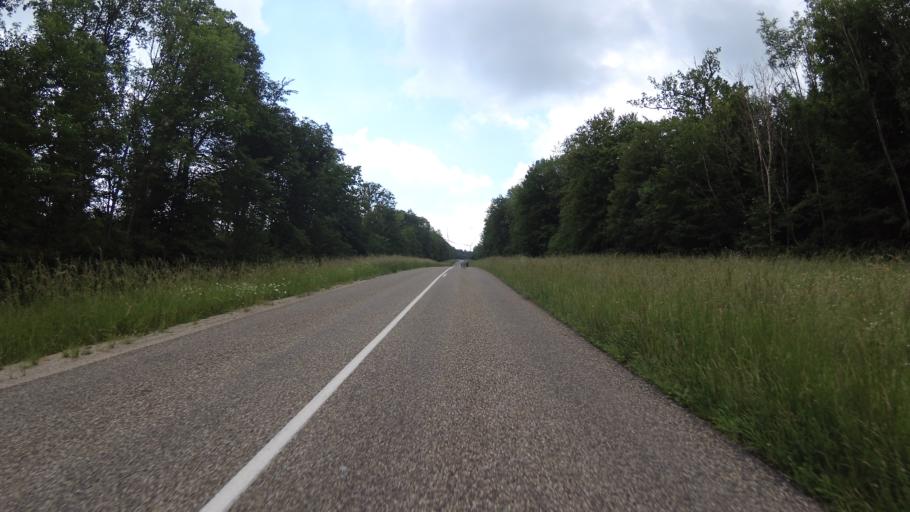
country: FR
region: Lorraine
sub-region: Departement de la Moselle
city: Remelfing
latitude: 49.0547
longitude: 7.0907
